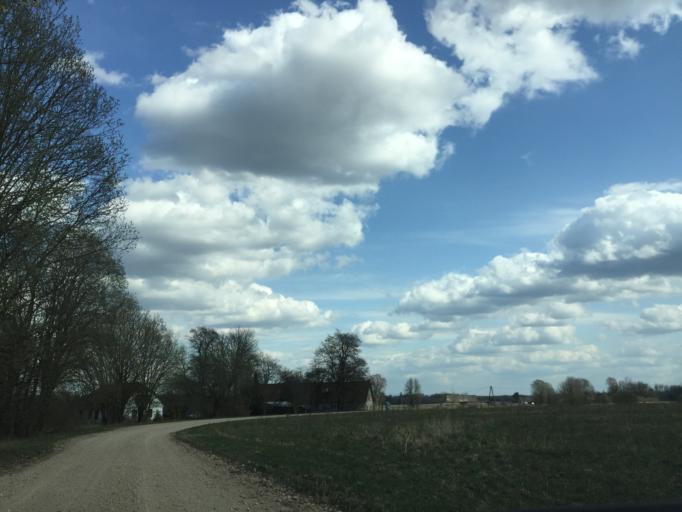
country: LV
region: Skriveri
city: Skriveri
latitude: 56.7613
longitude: 25.1321
